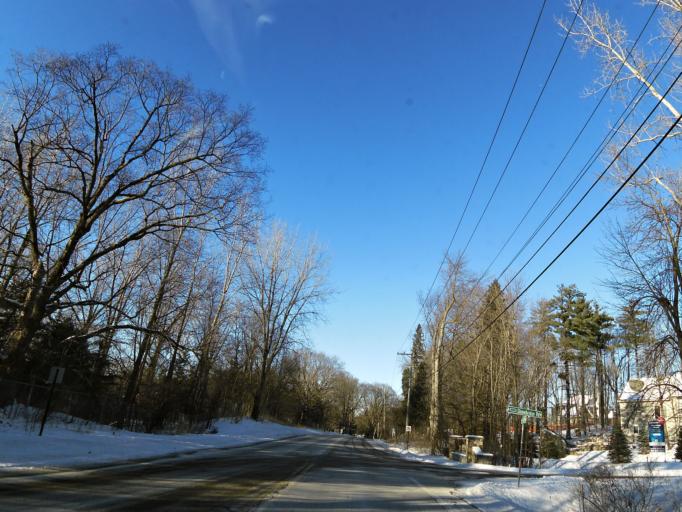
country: US
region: Minnesota
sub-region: Hennepin County
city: Mound
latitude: 44.9015
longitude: -93.6778
